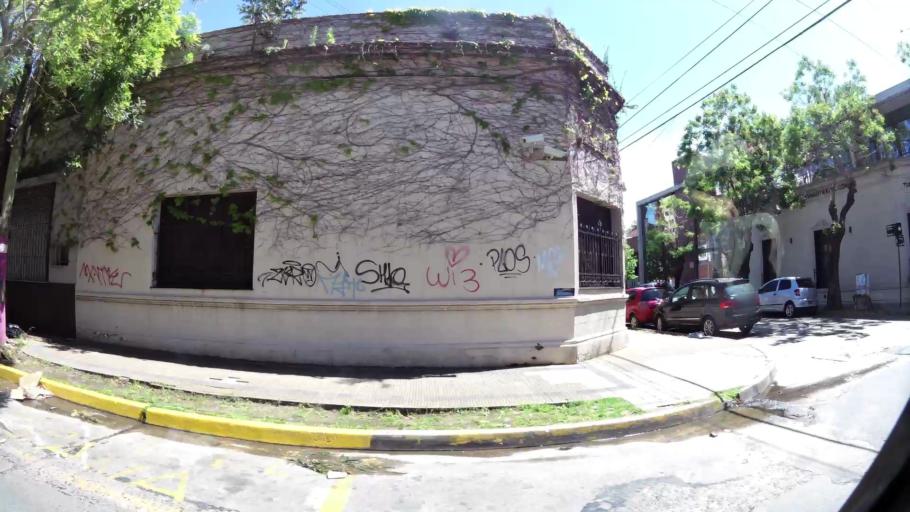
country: AR
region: Buenos Aires
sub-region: Partido de Quilmes
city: Quilmes
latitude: -34.7213
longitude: -58.2515
